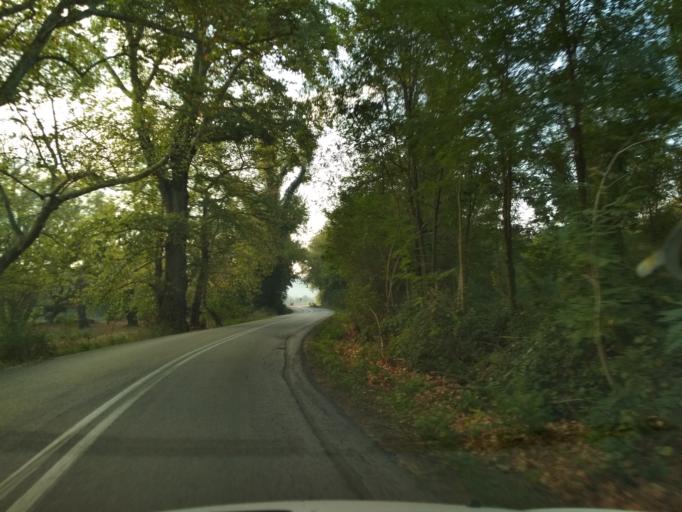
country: GR
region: Central Greece
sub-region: Nomos Evvoias
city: Prokopion
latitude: 38.7402
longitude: 23.4915
